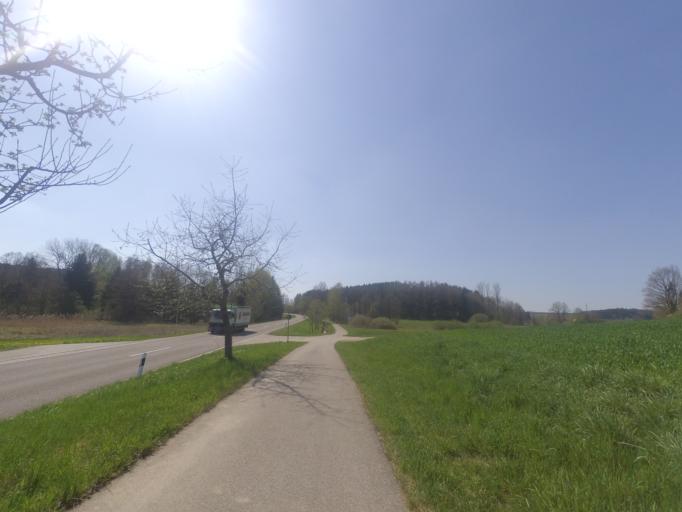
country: DE
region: Bavaria
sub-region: Swabia
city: Weissenhorn
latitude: 48.3267
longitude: 10.2105
